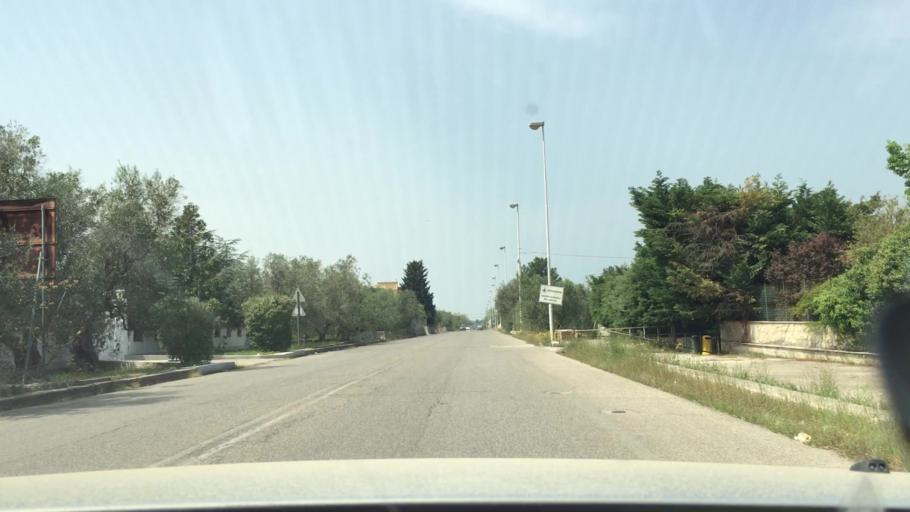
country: IT
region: Apulia
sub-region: Provincia di Barletta - Andria - Trani
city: Capirro
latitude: 41.2551
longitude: 16.4598
